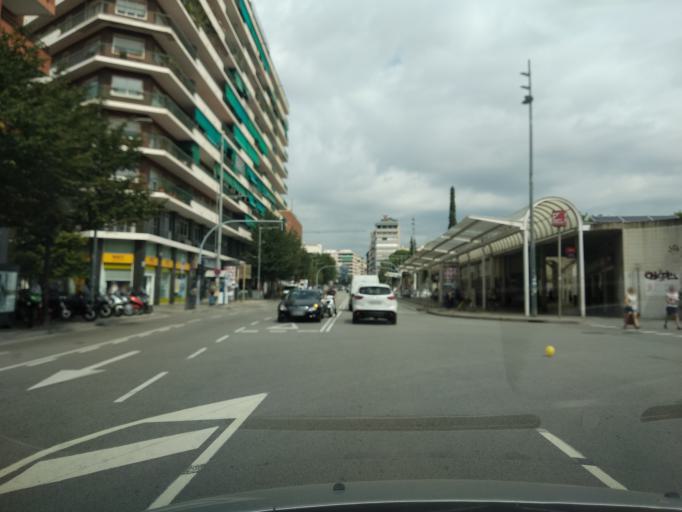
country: ES
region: Catalonia
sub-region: Provincia de Barcelona
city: Granollers
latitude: 41.6057
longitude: 2.2905
